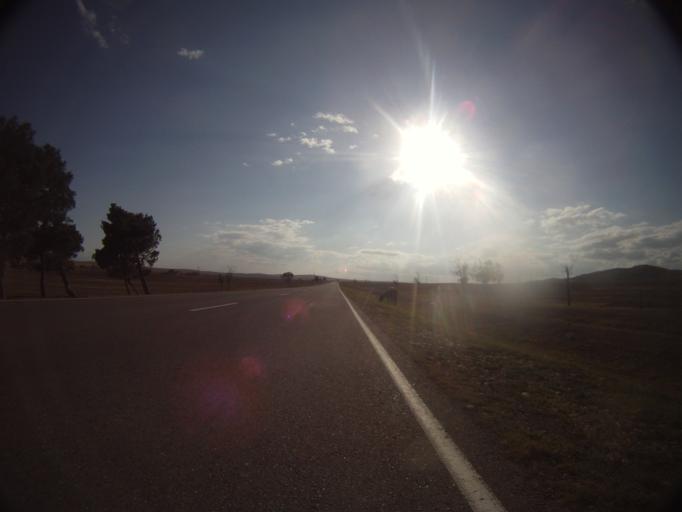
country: GE
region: Kvemo Kartli
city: Rust'avi
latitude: 41.5351
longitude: 44.9601
